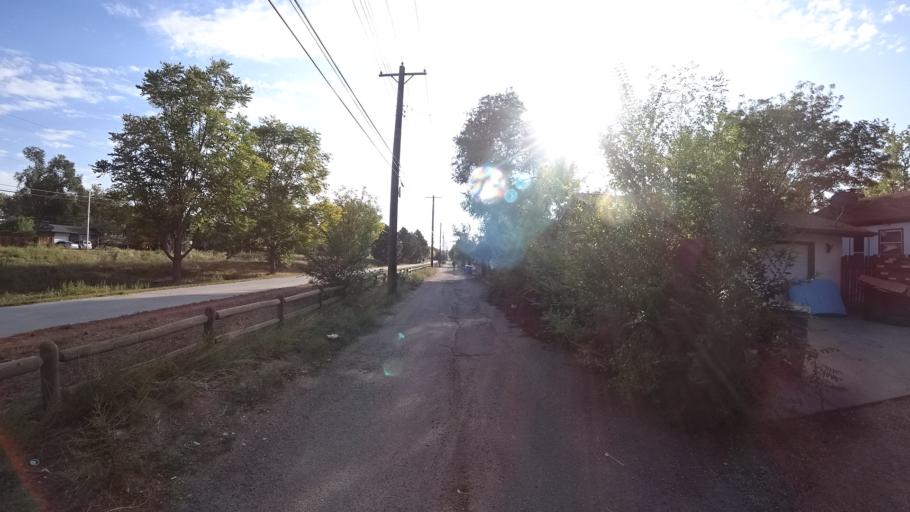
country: US
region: Colorado
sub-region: El Paso County
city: Colorado Springs
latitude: 38.8589
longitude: -104.7716
